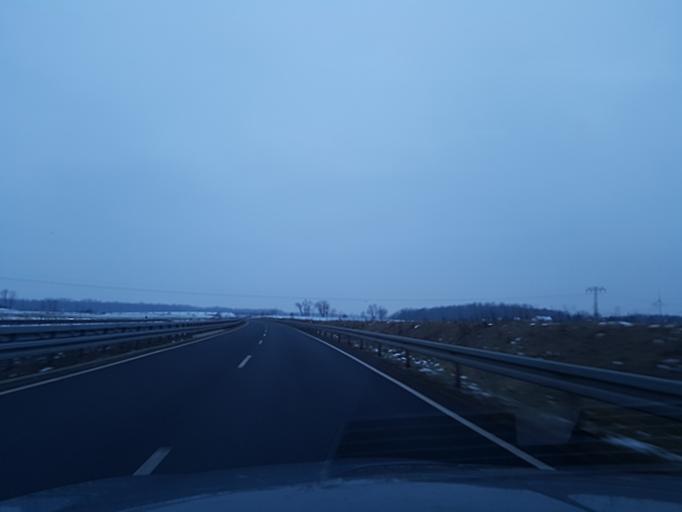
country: DE
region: Saxony
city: Riesa
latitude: 51.2829
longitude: 13.2556
